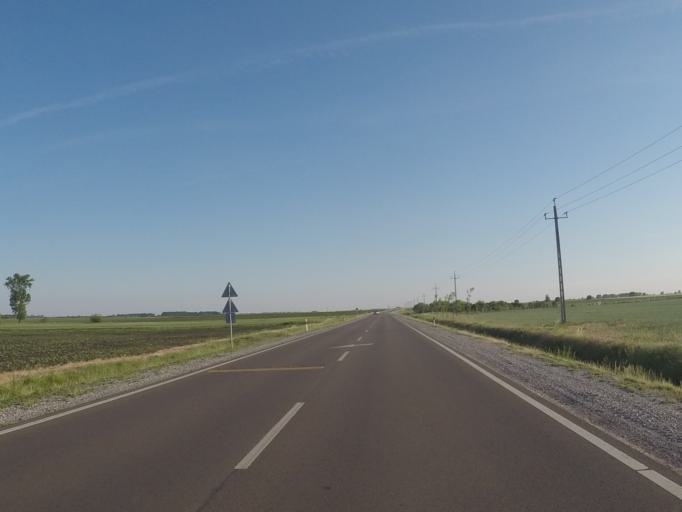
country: HU
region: Heves
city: Besenyotelek
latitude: 47.7151
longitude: 20.4124
